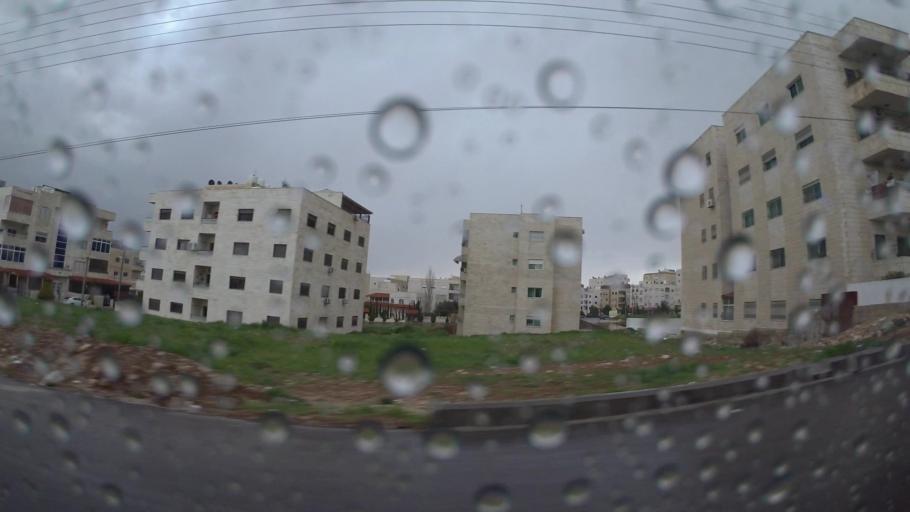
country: JO
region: Amman
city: Amman
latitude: 32.0056
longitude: 35.9550
